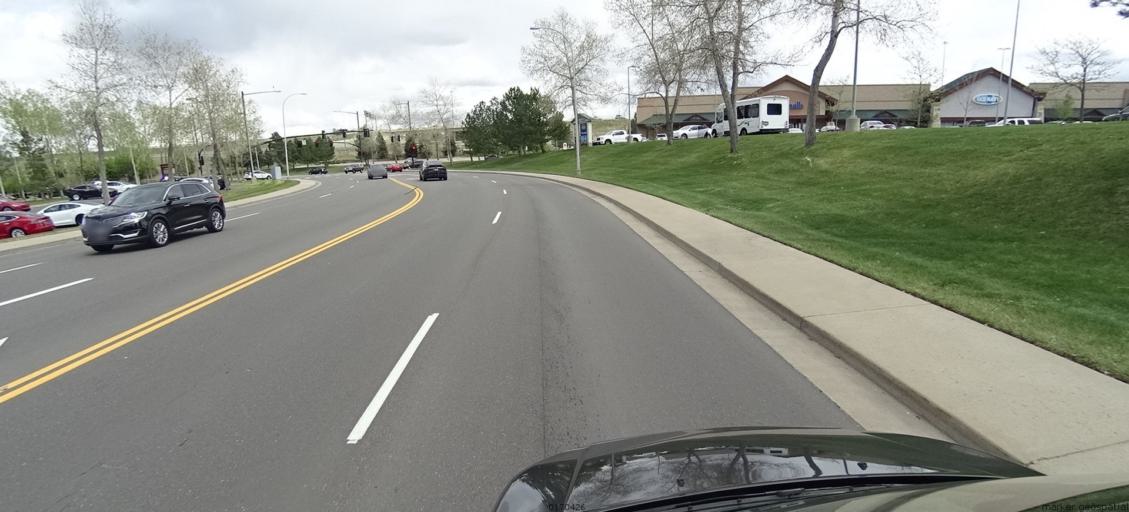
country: US
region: Colorado
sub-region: Adams County
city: Lone Tree
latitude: 39.5589
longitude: -104.8748
